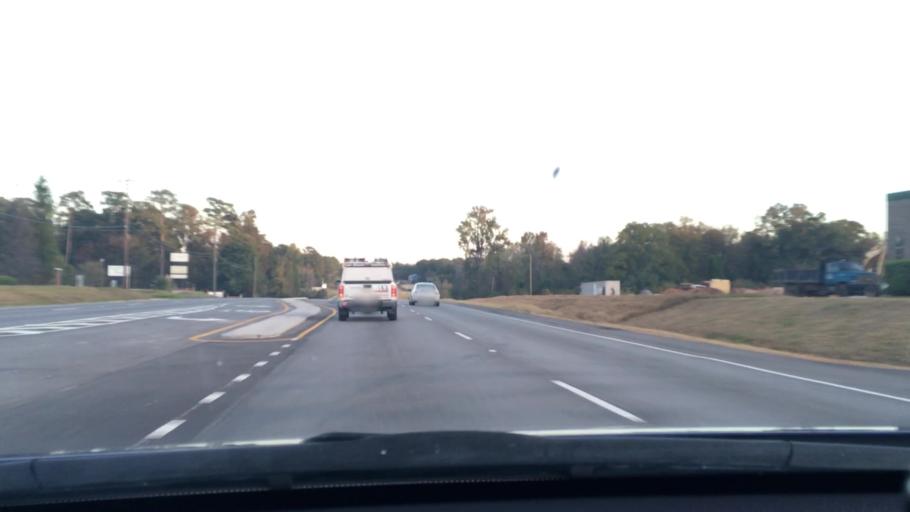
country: US
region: South Carolina
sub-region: Richland County
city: Hopkins
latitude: 33.9499
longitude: -80.9156
